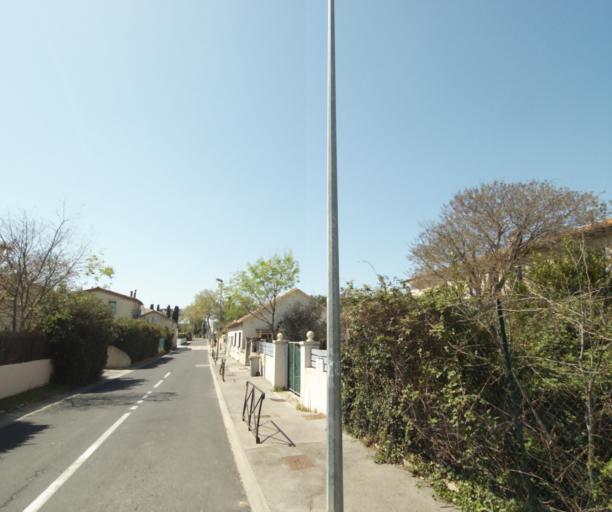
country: FR
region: Languedoc-Roussillon
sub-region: Departement de l'Herault
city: Montferrier-sur-Lez
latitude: 43.6662
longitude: 3.8569
